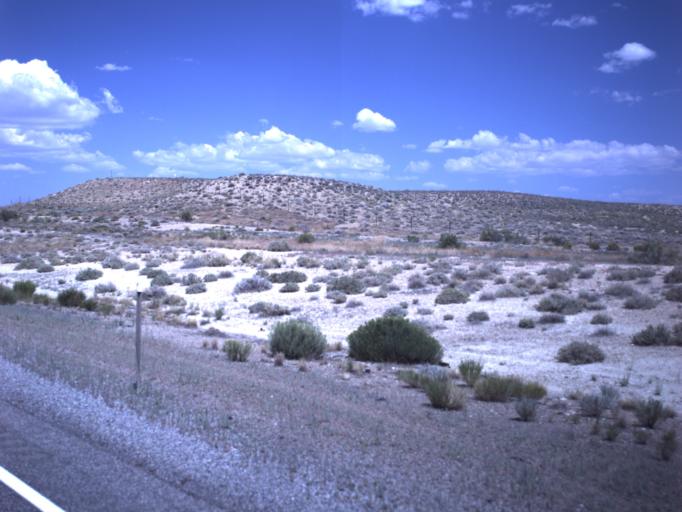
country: US
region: Utah
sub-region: Emery County
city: Huntington
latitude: 39.3762
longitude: -110.9127
